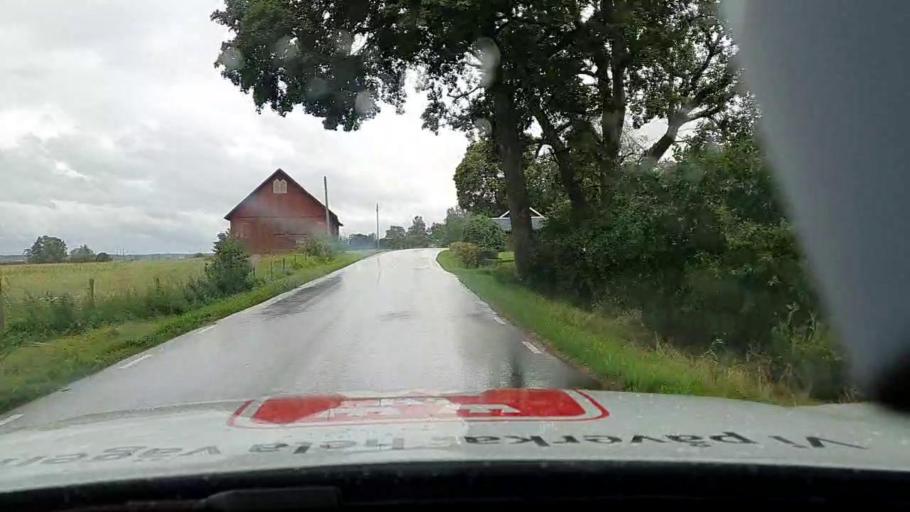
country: SE
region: Vaestra Goetaland
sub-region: Skovde Kommun
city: Stopen
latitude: 58.5524
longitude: 13.9777
